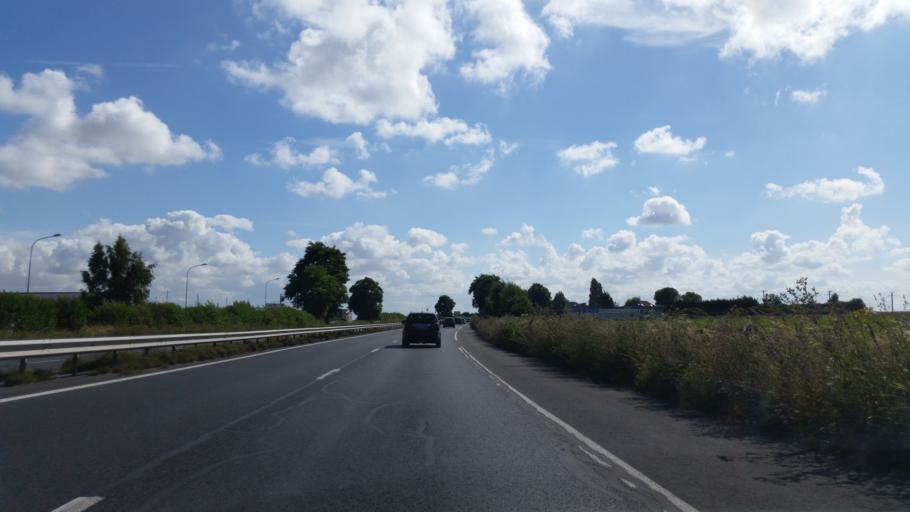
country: FR
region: Lower Normandy
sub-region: Departement du Calvados
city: Ouistreham
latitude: 49.2605
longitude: -0.2643
